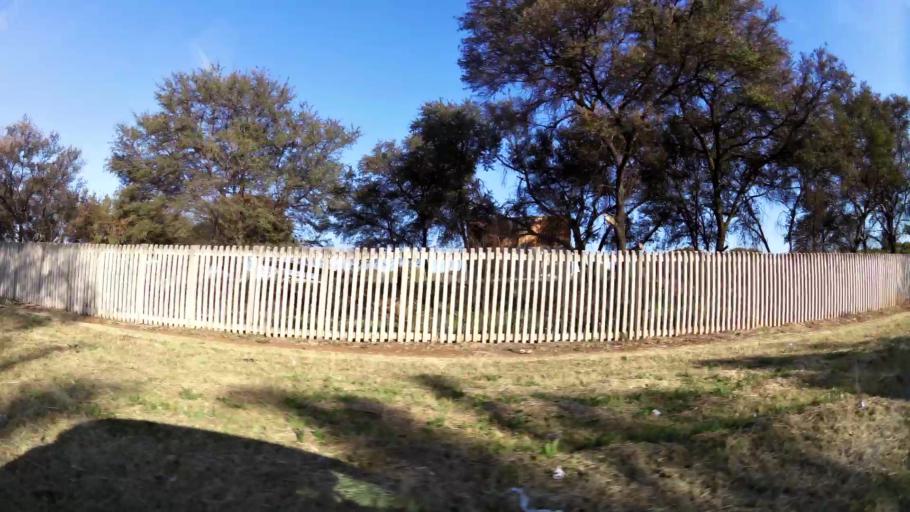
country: ZA
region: Gauteng
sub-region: City of Tshwane Metropolitan Municipality
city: Pretoria
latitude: -25.7591
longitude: 28.1187
